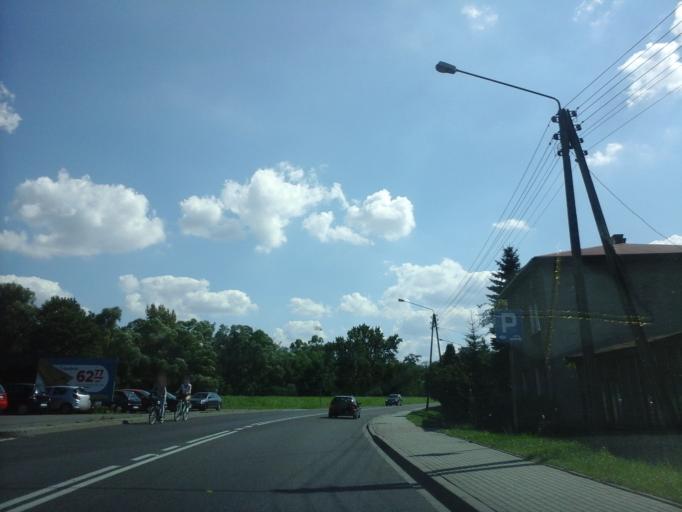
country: PL
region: Lesser Poland Voivodeship
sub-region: Powiat oswiecimski
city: Oswiecim
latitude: 50.0318
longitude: 19.2101
